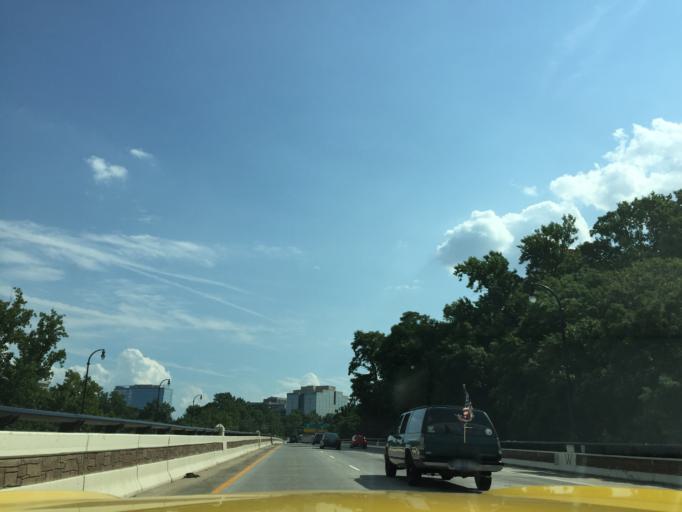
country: US
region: Delaware
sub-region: New Castle County
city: Wilmington
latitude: 39.7562
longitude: -75.5527
